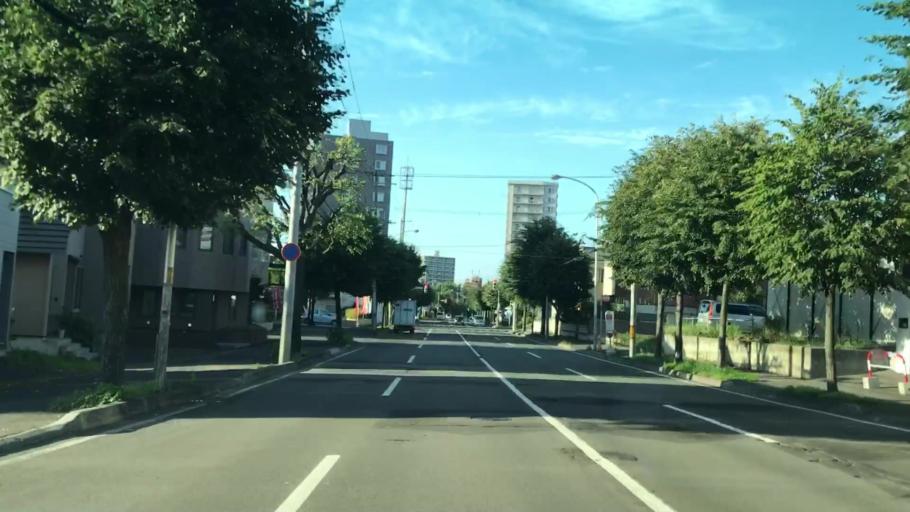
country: JP
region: Hokkaido
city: Sapporo
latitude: 43.0435
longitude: 141.3639
